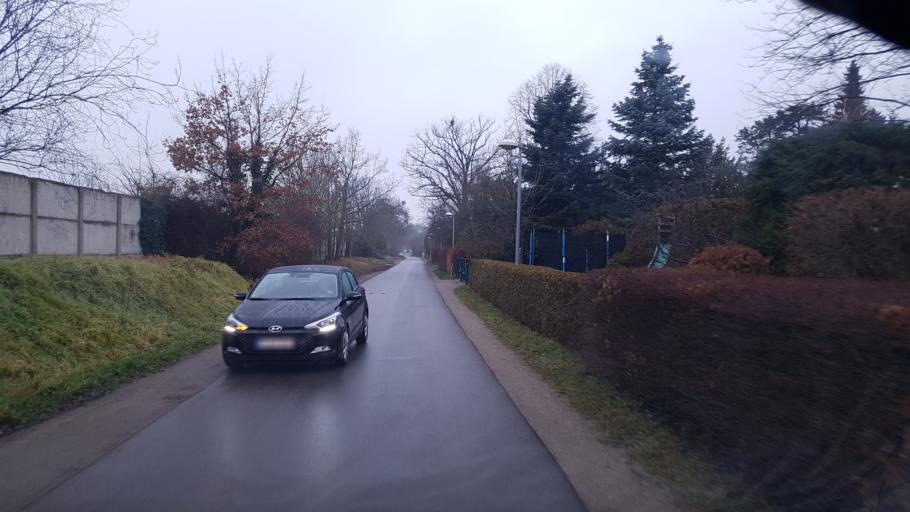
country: DE
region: Brandenburg
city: Stahnsdorf
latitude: 52.3738
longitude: 13.2129
